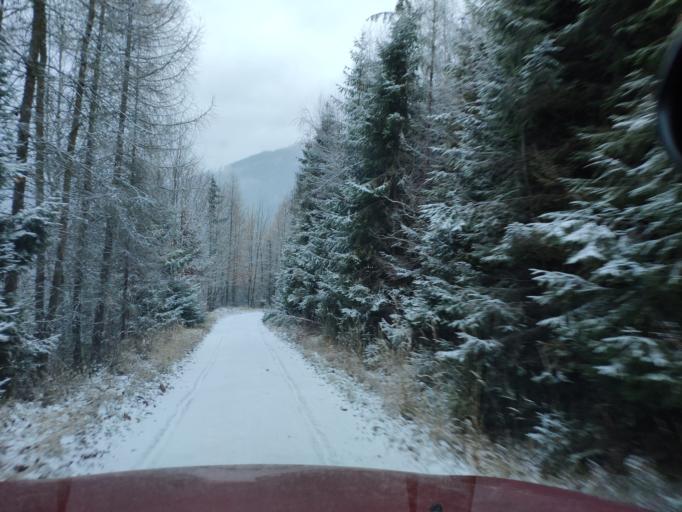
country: SK
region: Kosicky
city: Spisska Nova Ves
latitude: 48.8127
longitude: 20.5149
